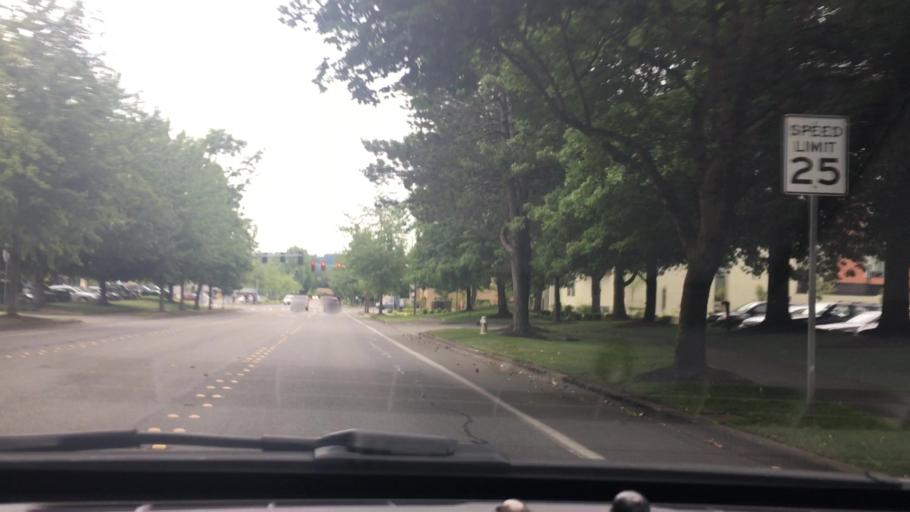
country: US
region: Washington
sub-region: King County
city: Issaquah
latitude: 47.5419
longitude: -122.0575
